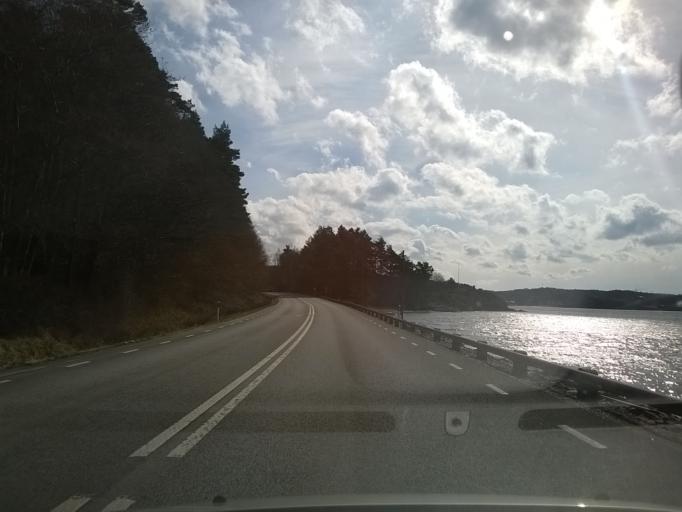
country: SE
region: Vaestra Goetaland
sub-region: Orust
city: Henan
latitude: 58.2543
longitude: 11.6787
